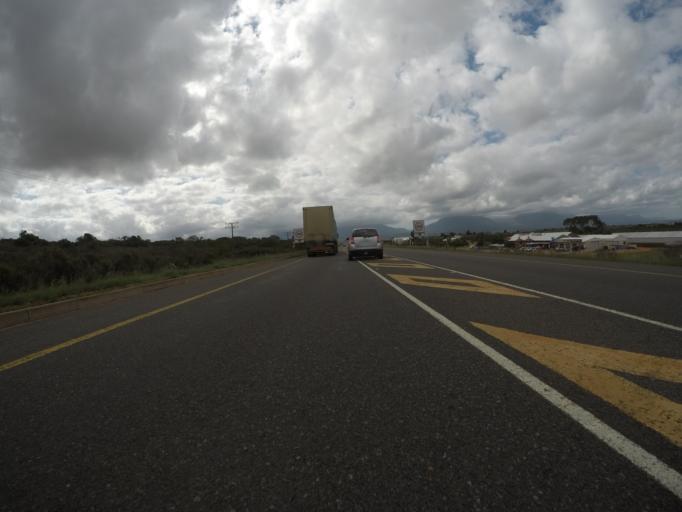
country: ZA
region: Western Cape
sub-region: Eden District Municipality
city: Riversdale
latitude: -34.1128
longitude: 21.2539
